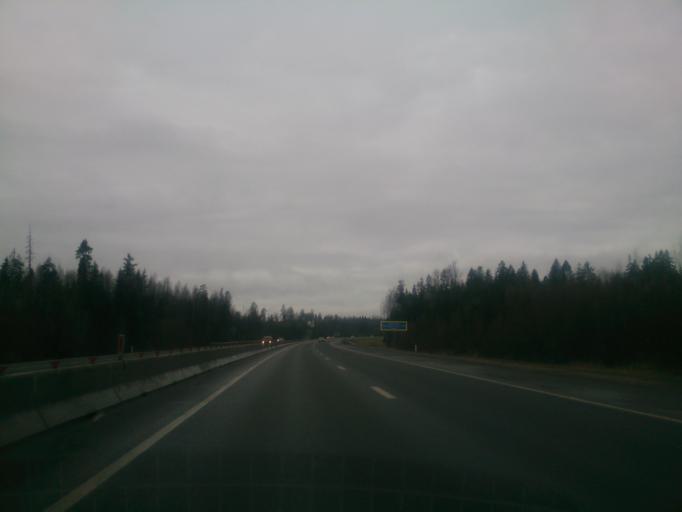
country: RU
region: Leningrad
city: Tosno
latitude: 59.4872
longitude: 30.9141
